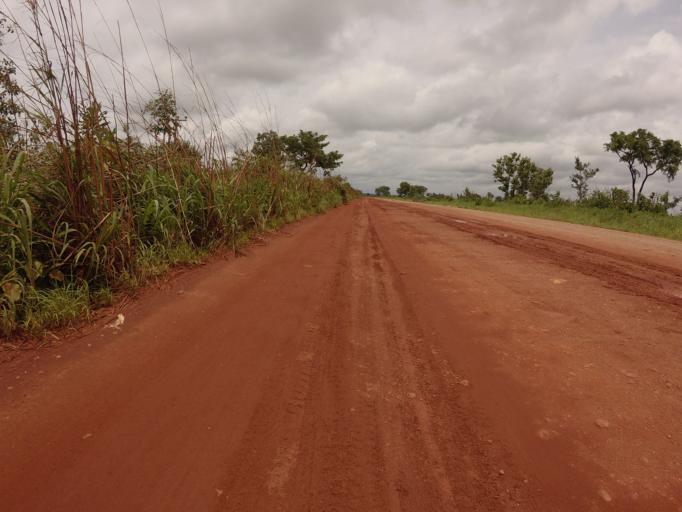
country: GH
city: Kpandae
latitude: 8.4491
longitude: 0.3505
